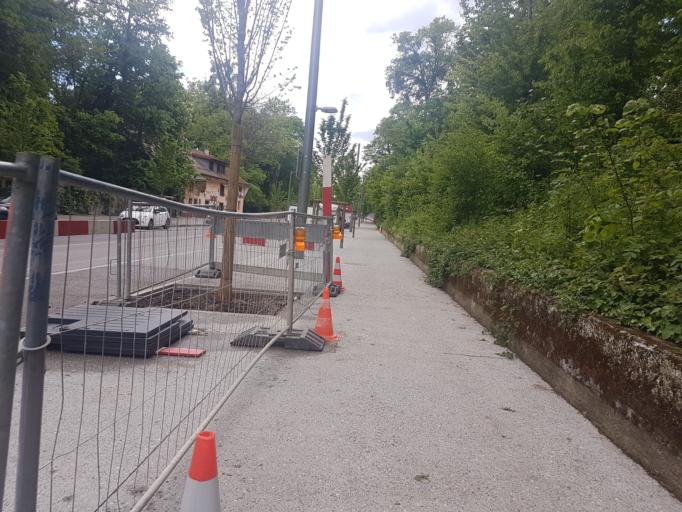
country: CH
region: Geneva
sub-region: Geneva
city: Versoix
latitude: 46.2951
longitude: 6.1668
